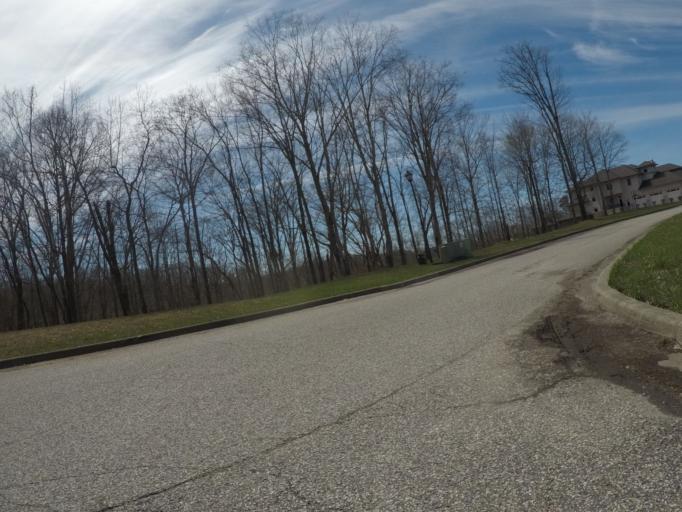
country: US
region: West Virginia
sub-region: Cabell County
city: Barboursville
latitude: 38.4023
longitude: -82.3062
